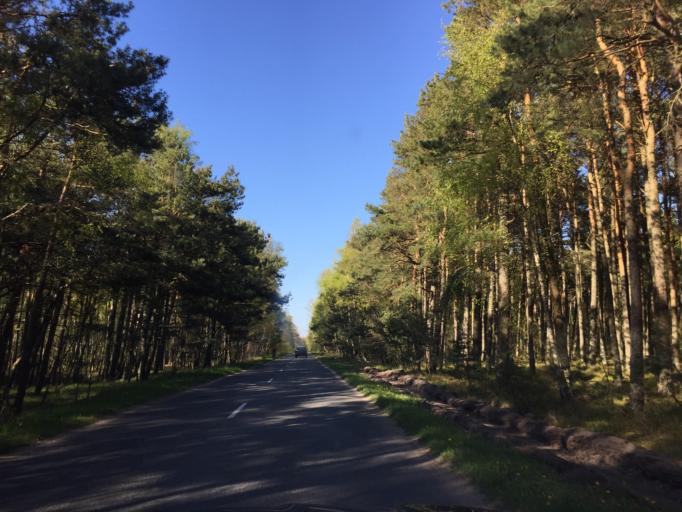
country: LT
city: Nida
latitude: 55.2080
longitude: 20.8766
